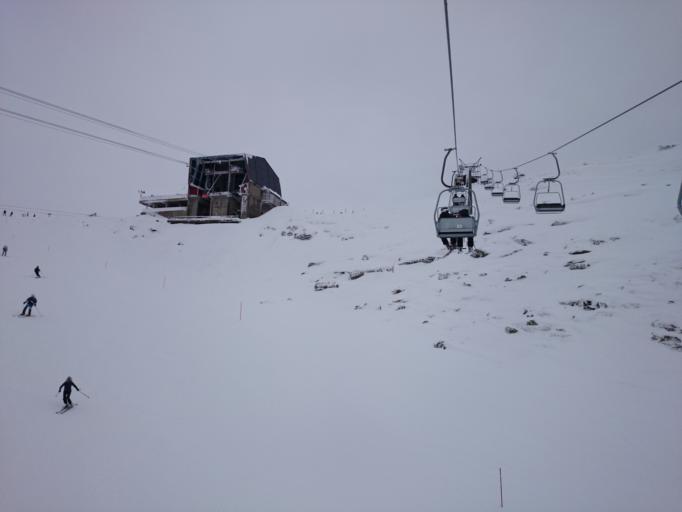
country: SE
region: Jaemtland
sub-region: Are Kommun
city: Are
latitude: 63.4259
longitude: 13.0808
